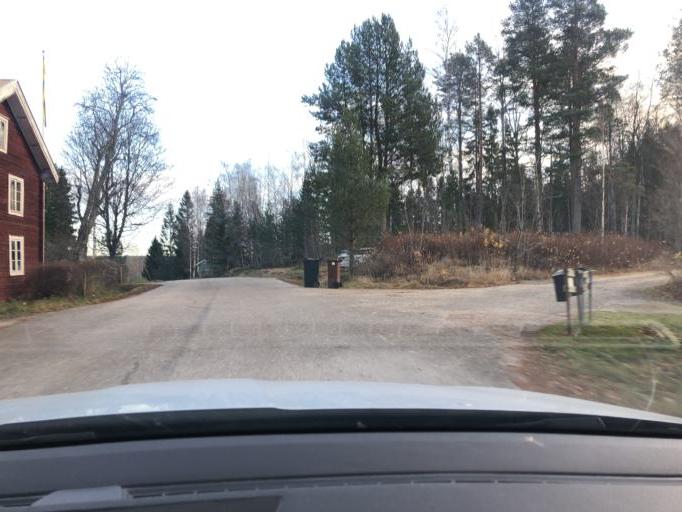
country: SE
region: Gaevleborg
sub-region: Hudiksvalls Kommun
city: Sorforsa
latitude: 61.7127
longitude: 16.9388
